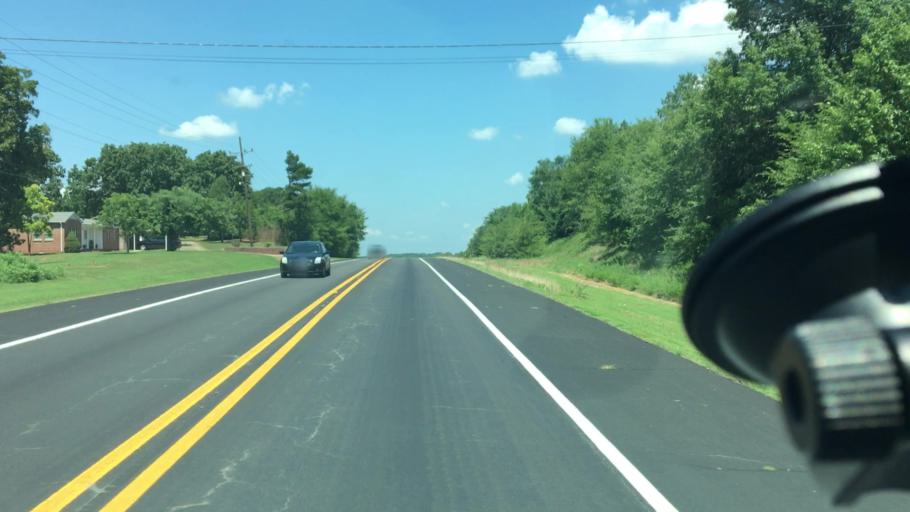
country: US
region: Arkansas
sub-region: Sebastian County
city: Lavaca
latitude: 35.2997
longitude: -94.1579
